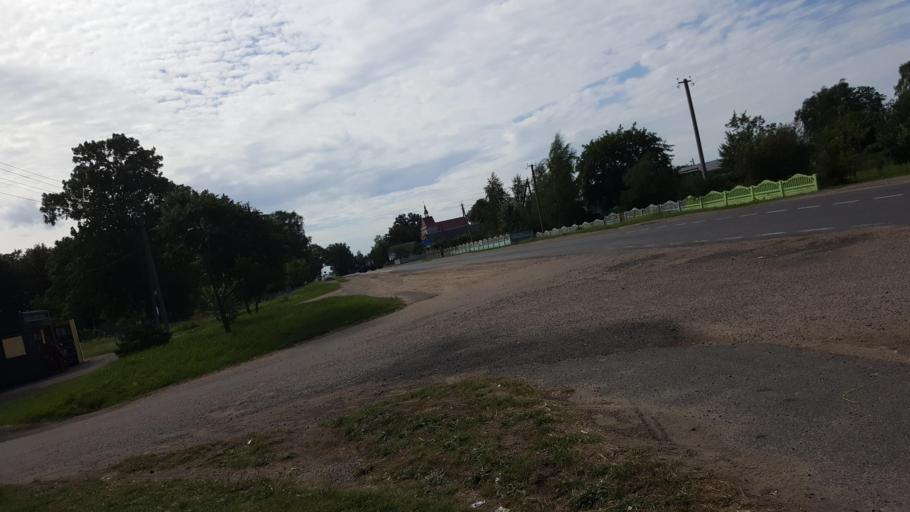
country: BY
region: Brest
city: Kamyanyets
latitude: 52.3180
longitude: 23.9201
